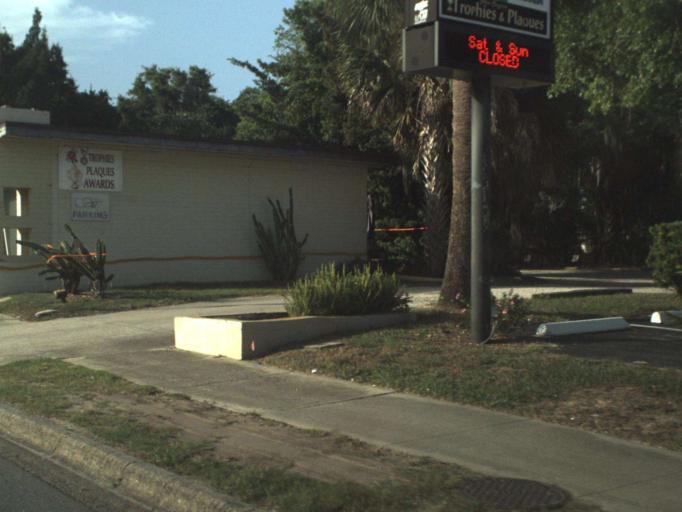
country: US
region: Florida
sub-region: Volusia County
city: New Smyrna Beach
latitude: 29.0403
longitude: -80.9337
